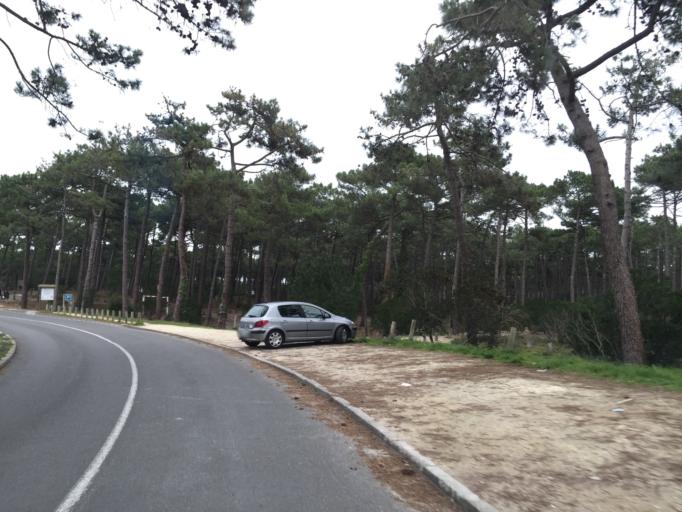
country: FR
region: Aquitaine
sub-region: Departement de la Gironde
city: Lacanau
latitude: 45.0082
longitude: -1.1953
